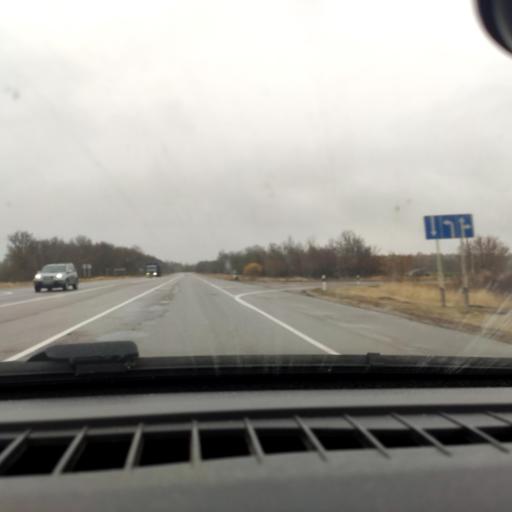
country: RU
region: Voronezj
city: Kolodeznyy
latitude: 51.3097
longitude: 39.0352
